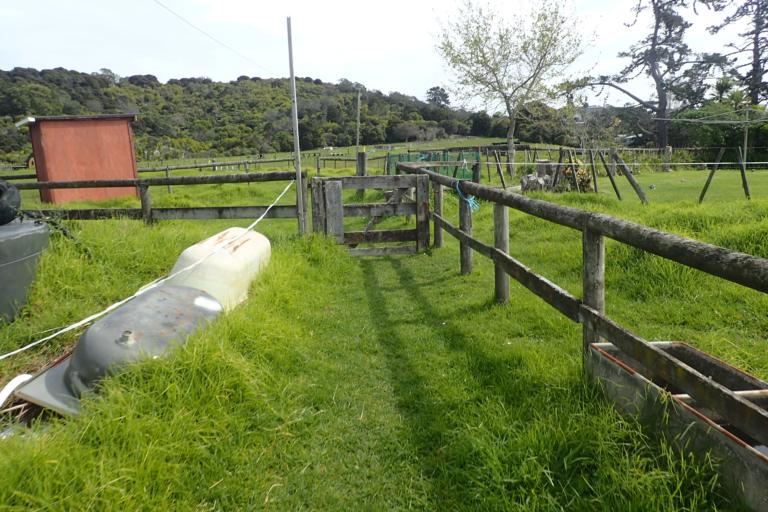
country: NZ
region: Auckland
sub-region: Auckland
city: Pakuranga
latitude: -36.7886
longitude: 175.0083
